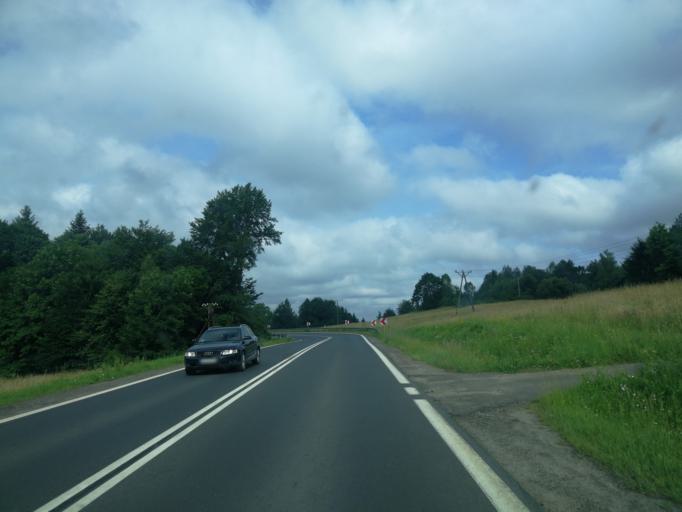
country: PL
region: Subcarpathian Voivodeship
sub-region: Powiat leski
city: Uherce Mineralne
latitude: 49.4682
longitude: 22.3816
